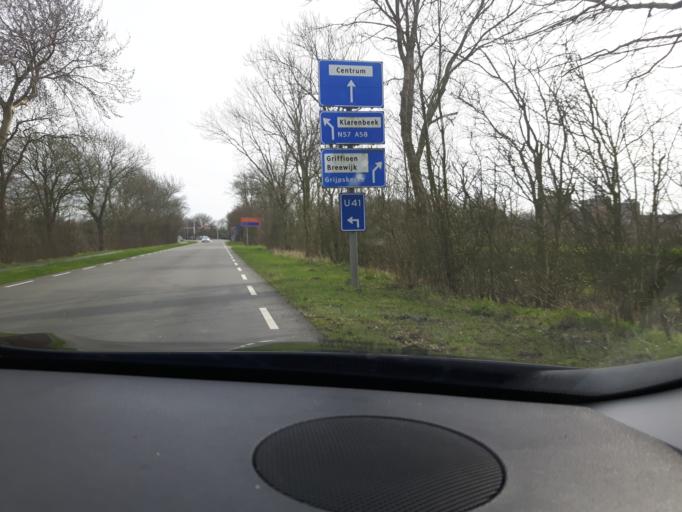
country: NL
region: Zeeland
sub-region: Gemeente Middelburg
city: Middelburg
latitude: 51.5088
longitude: 3.6004
